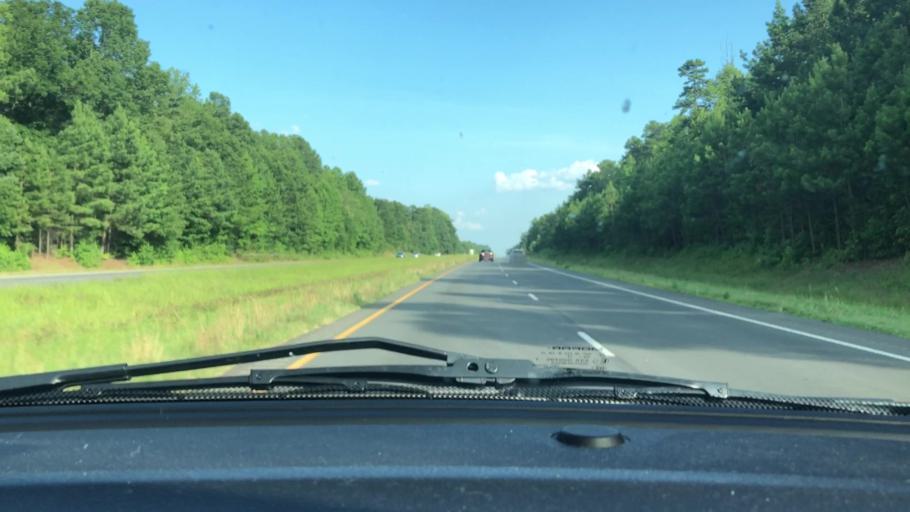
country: US
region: North Carolina
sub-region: Chatham County
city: Siler City
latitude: 35.6419
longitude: -79.3793
